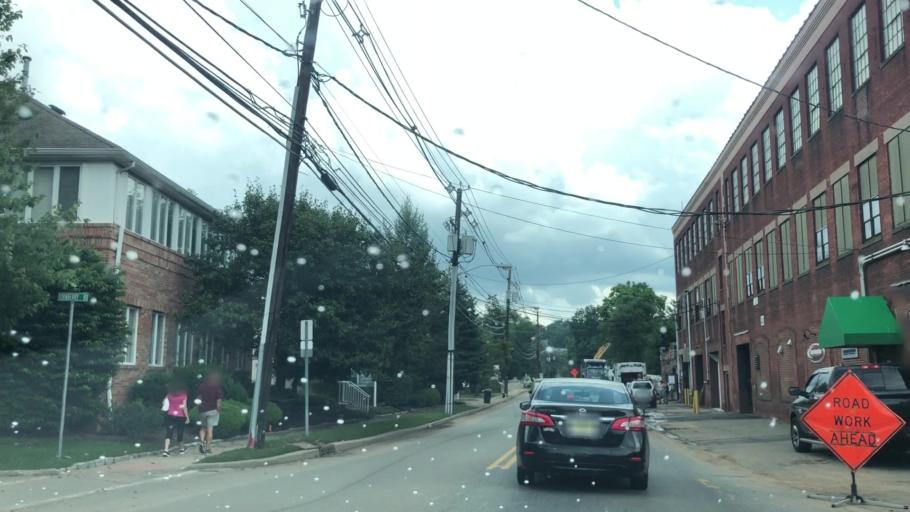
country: US
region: New Jersey
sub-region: Passaic County
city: Little Falls
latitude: 40.8787
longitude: -74.2209
